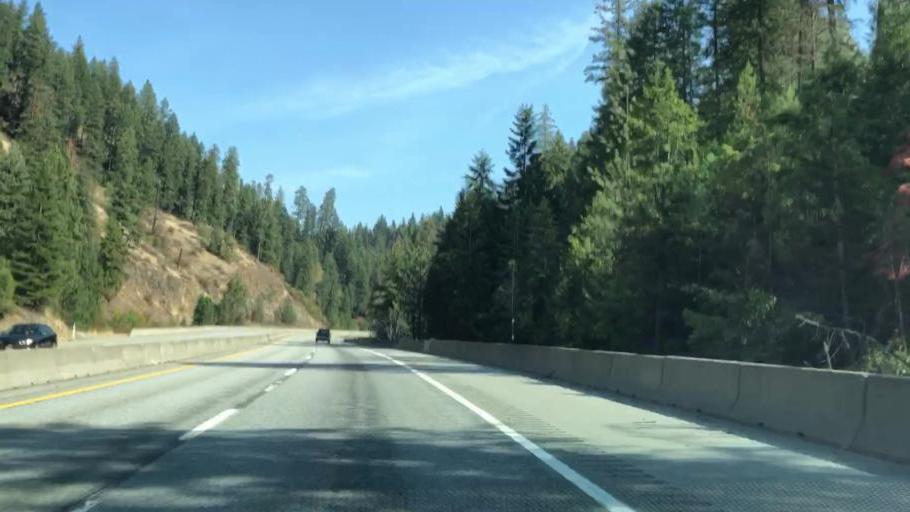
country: US
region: Idaho
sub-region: Kootenai County
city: Coeur d'Alene
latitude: 47.6270
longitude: -116.5929
